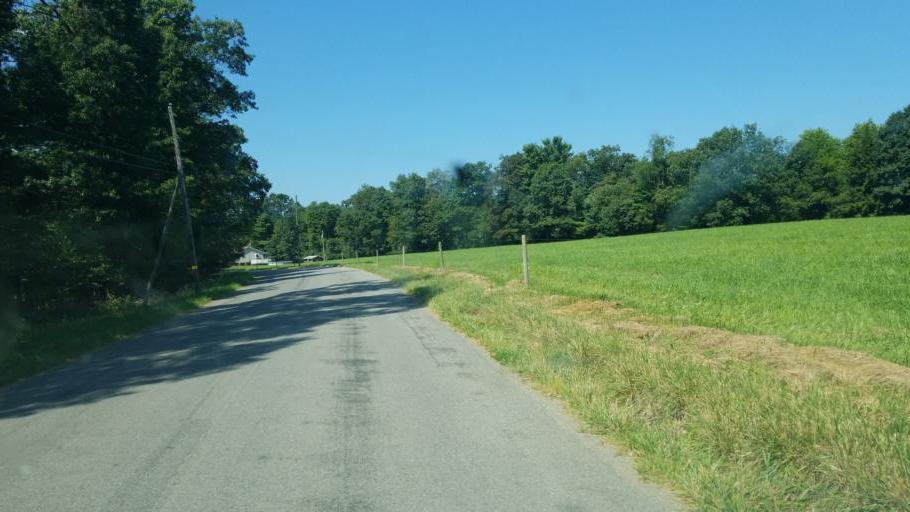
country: US
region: Pennsylvania
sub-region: Clarion County
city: Clarion
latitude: 41.1733
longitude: -79.4204
